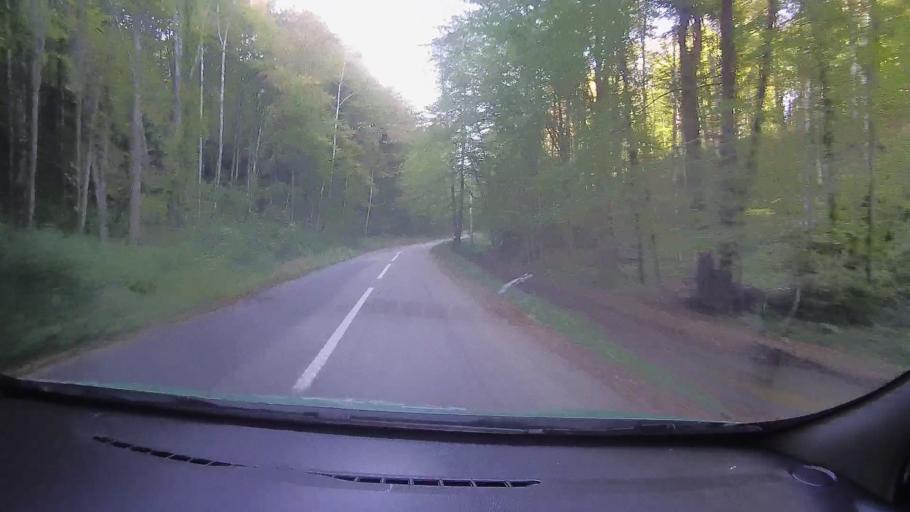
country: RO
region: Timis
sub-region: Comuna Nadrag
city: Nadrag
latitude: 45.6745
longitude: 22.1762
